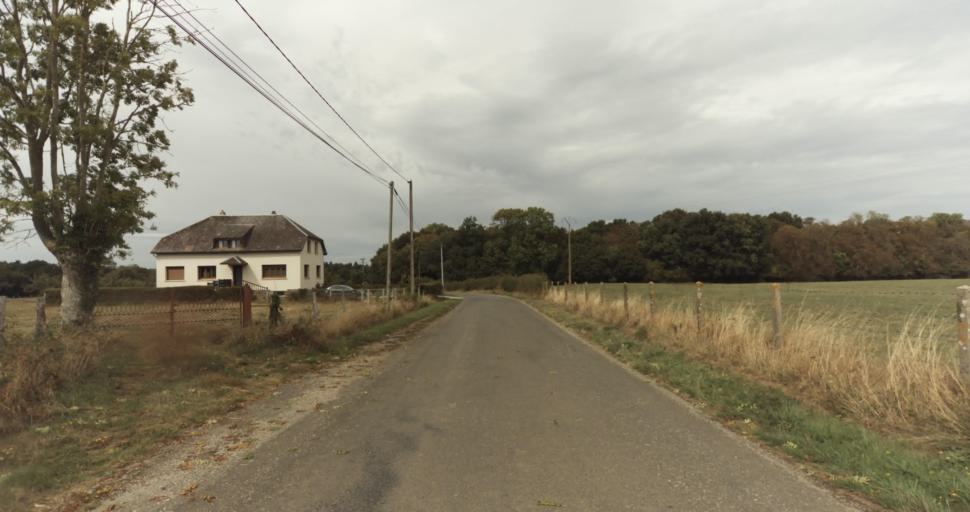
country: FR
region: Lower Normandy
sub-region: Departement du Calvados
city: Orbec
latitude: 48.9449
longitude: 0.3759
